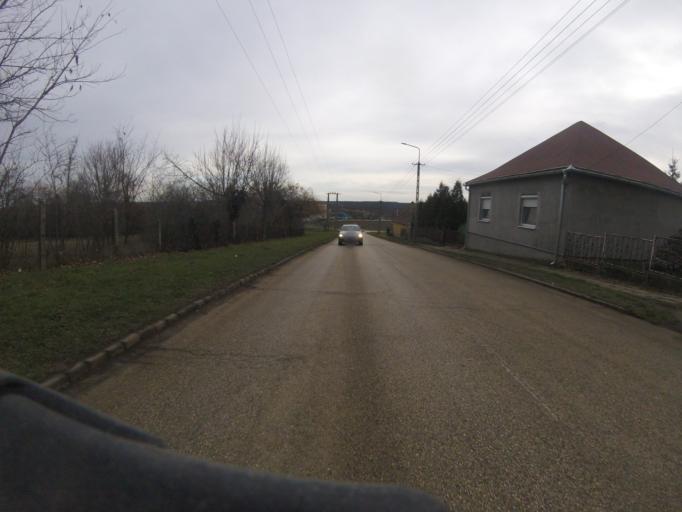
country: HU
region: Tolna
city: Dombovar
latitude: 46.3881
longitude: 18.1665
